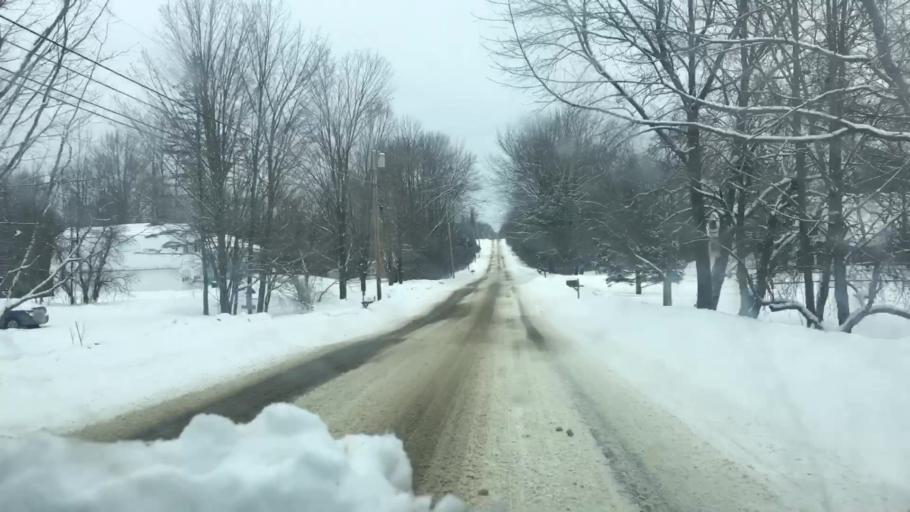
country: US
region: Maine
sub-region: Penobscot County
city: Bradford
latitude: 45.0114
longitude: -68.9950
